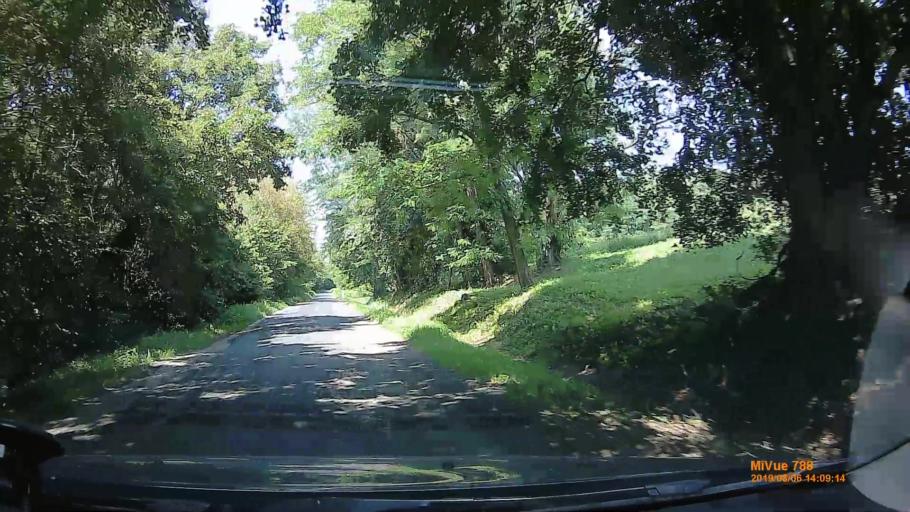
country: HU
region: Zala
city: Zalakomar
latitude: 46.5385
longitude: 17.0829
